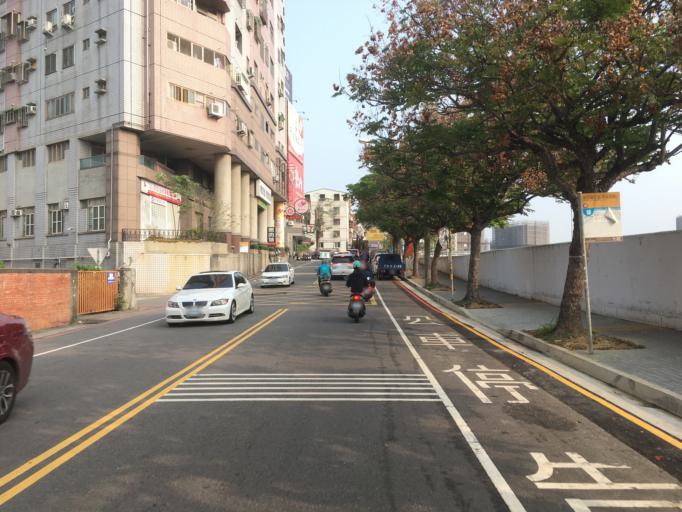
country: TW
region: Taiwan
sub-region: Taichung City
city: Taichung
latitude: 24.1685
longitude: 120.7051
